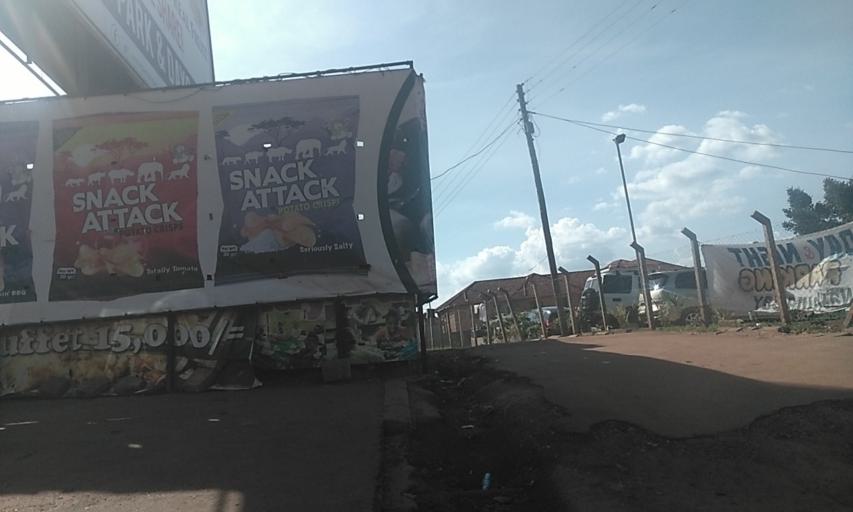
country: UG
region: Central Region
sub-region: Wakiso District
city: Kireka
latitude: 0.3728
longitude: 32.6244
